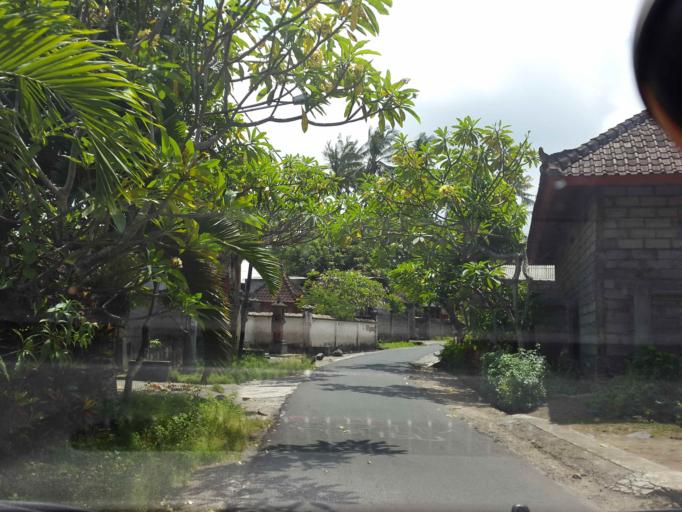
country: ID
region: Bali
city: Klungkung
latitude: -8.5535
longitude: 115.3844
